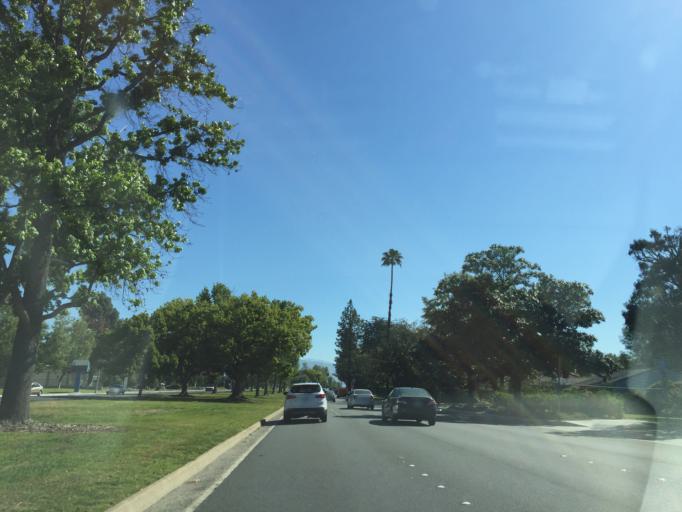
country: US
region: California
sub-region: Los Angeles County
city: San Marino
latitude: 34.1243
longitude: -118.0993
